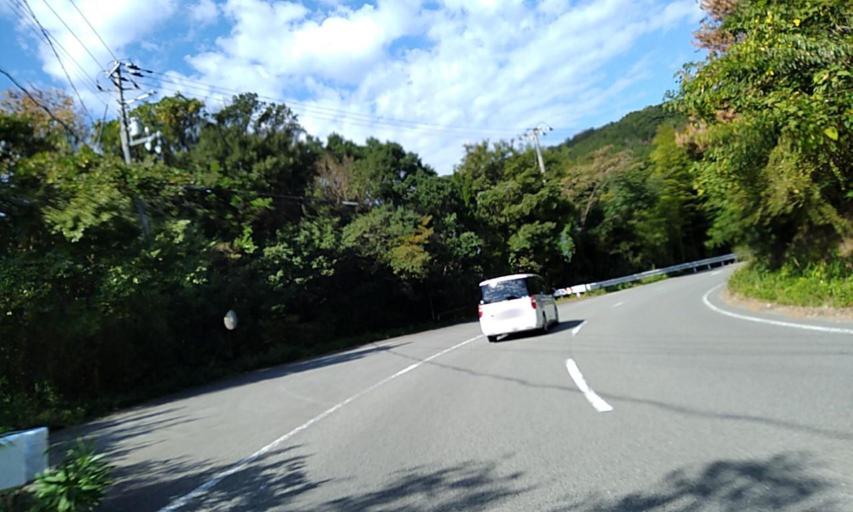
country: JP
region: Wakayama
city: Gobo
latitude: 33.9667
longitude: 135.1182
